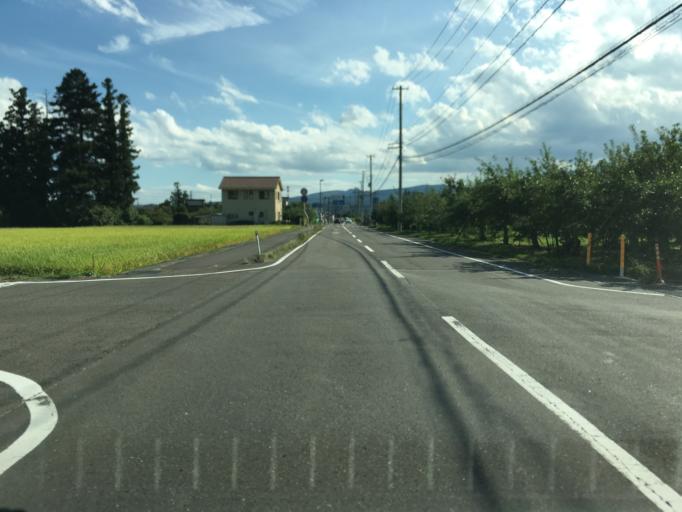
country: JP
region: Fukushima
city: Fukushima-shi
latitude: 37.7605
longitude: 140.4206
